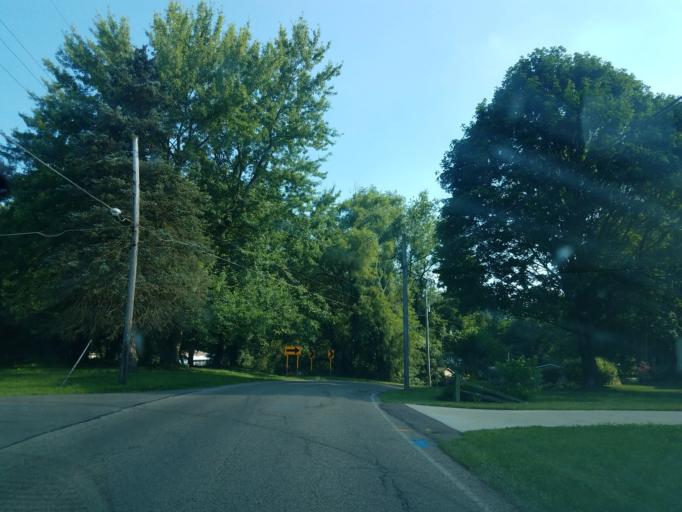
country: US
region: Ohio
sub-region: Stark County
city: Uniontown
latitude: 40.9736
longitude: -81.4137
